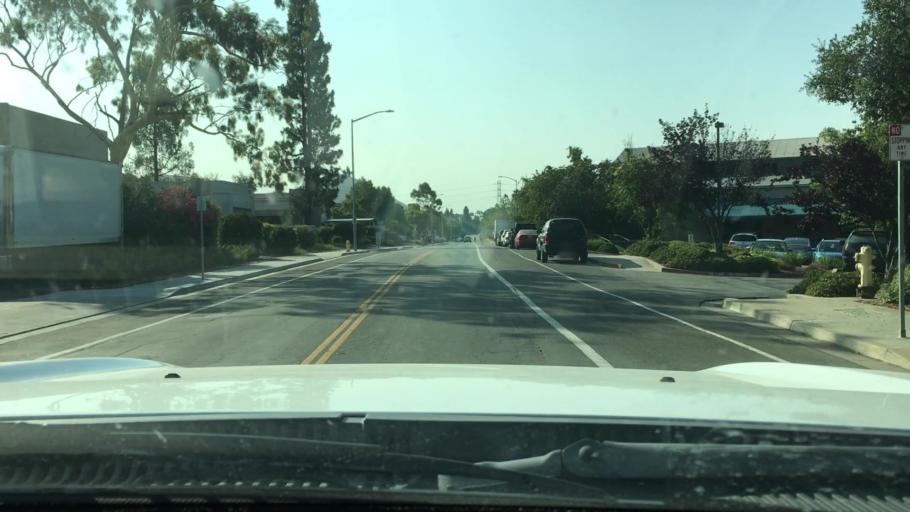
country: US
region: California
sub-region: San Luis Obispo County
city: San Luis Obispo
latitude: 35.2588
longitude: -120.6468
